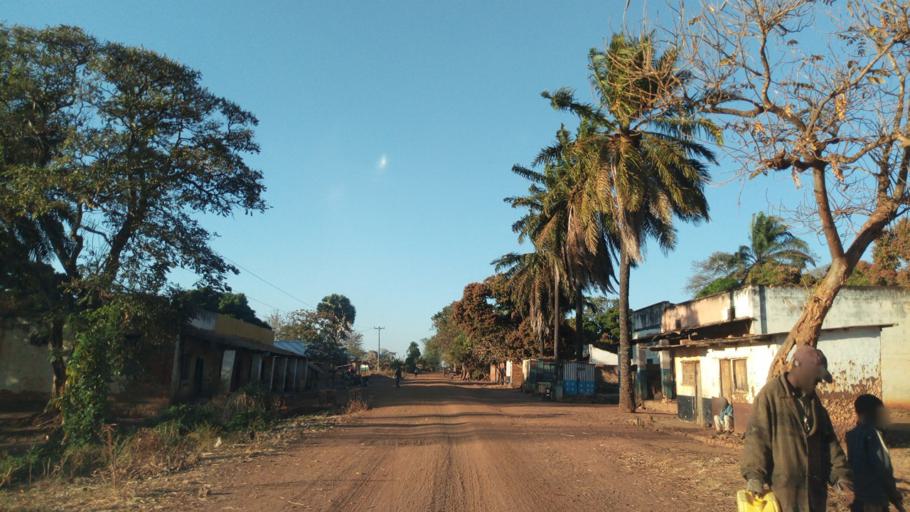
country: ZM
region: Luapula
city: Mwense
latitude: -10.3673
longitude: 28.6153
